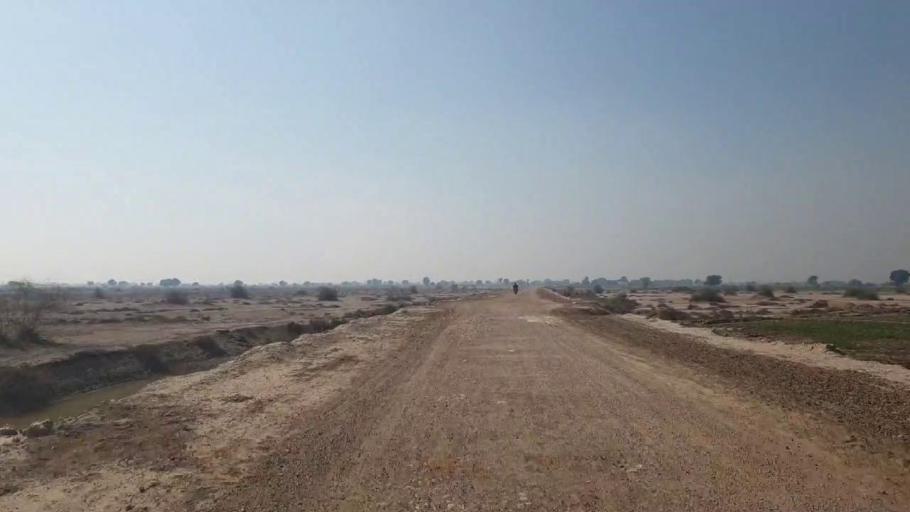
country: PK
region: Sindh
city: Shahpur Chakar
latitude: 26.1141
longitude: 68.6099
